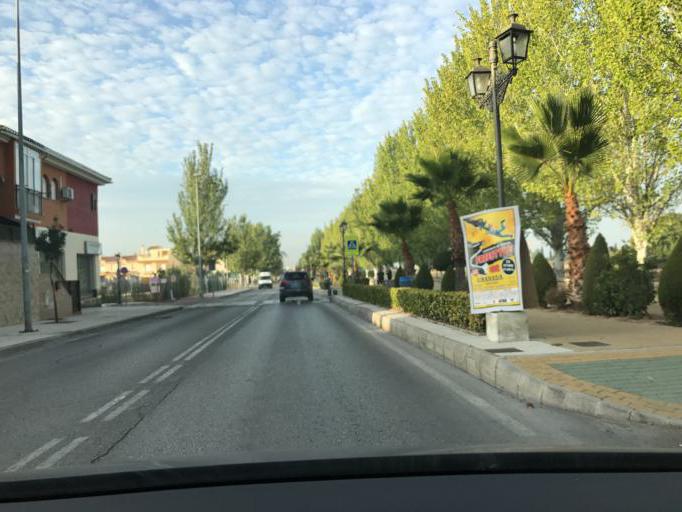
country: ES
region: Andalusia
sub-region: Provincia de Granada
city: Peligros
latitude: 37.2327
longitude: -3.6329
